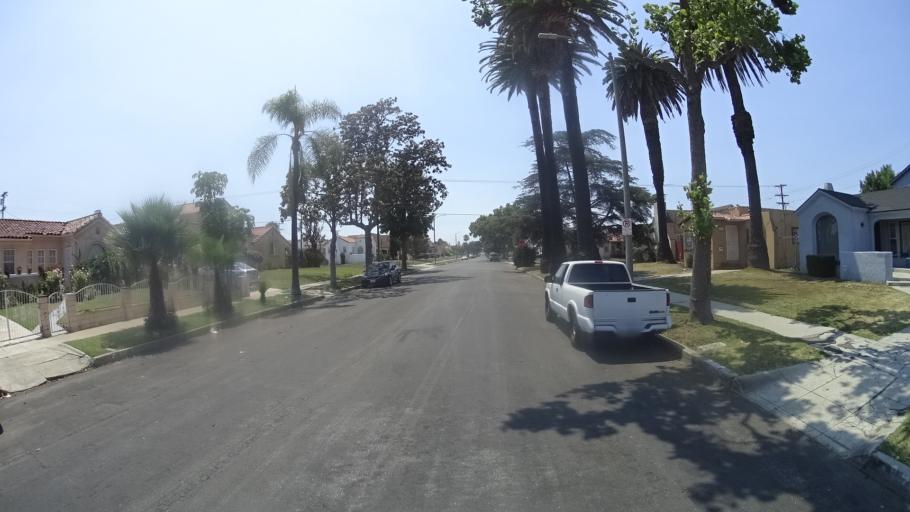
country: US
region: California
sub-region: Los Angeles County
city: Westmont
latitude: 33.9692
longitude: -118.3149
